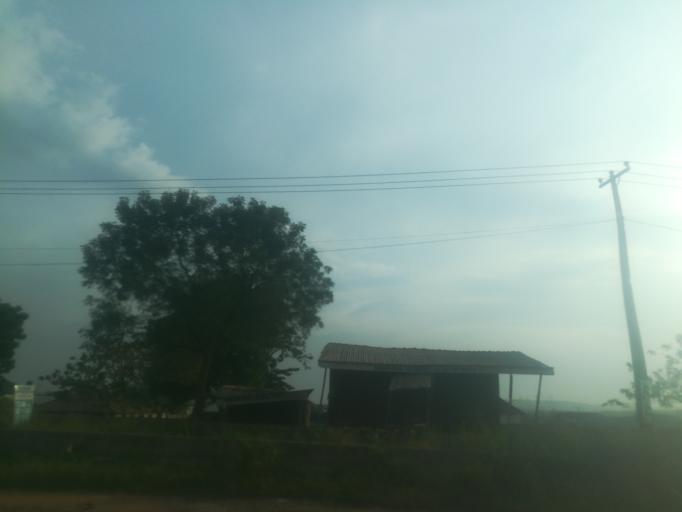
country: NG
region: Ogun
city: Abeokuta
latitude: 7.1677
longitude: 3.3004
